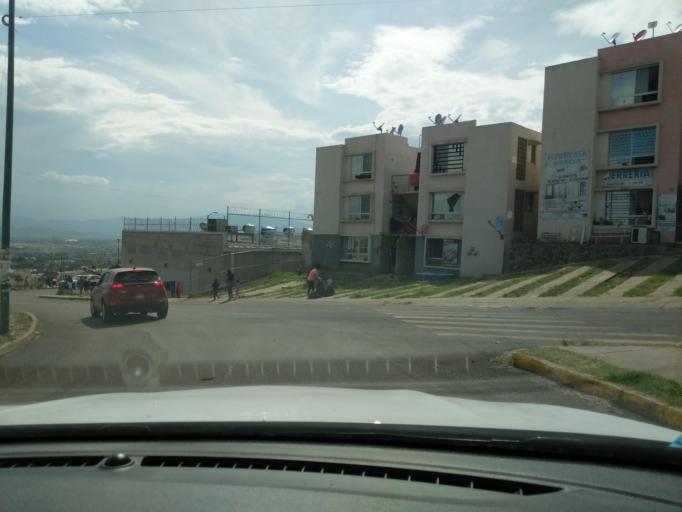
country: MX
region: Jalisco
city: San Jose del Castillo
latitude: 20.5221
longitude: -103.2258
